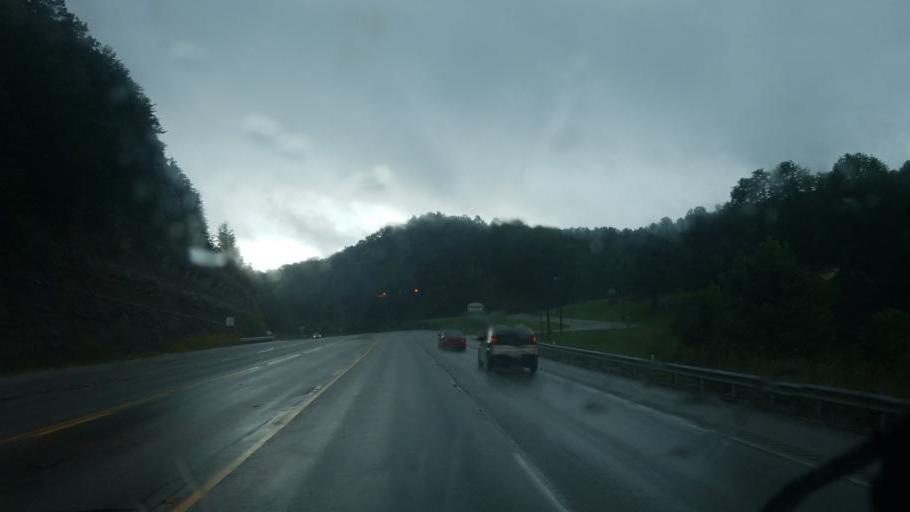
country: US
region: Kentucky
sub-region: Rowan County
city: Morehead
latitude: 38.1825
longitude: -83.4693
